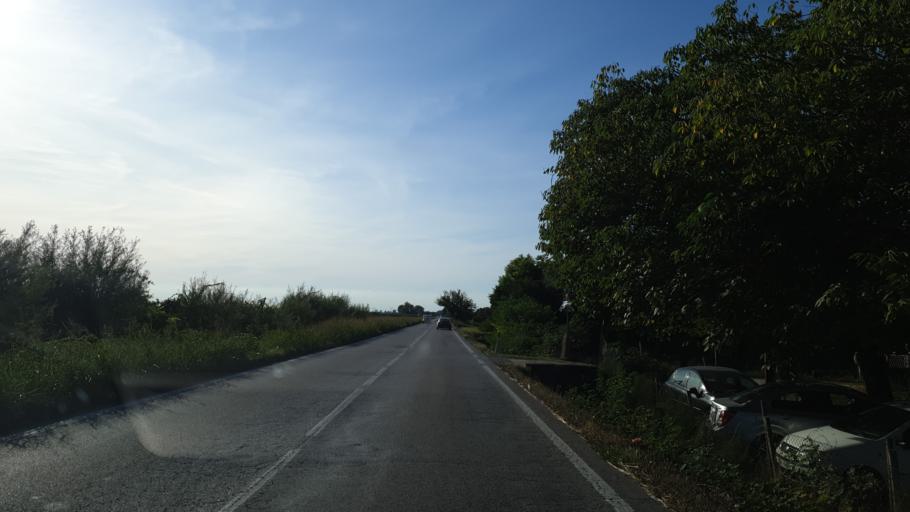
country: IT
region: Emilia-Romagna
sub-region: Provincia di Ravenna
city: Voltana
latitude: 44.5453
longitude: 11.9748
